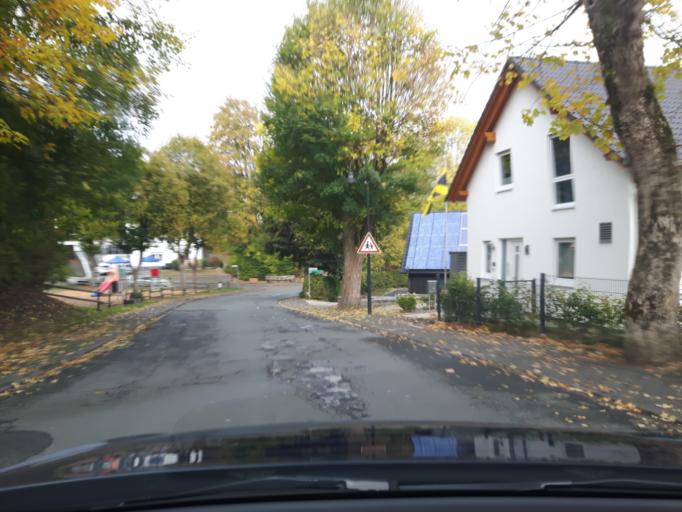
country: DE
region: North Rhine-Westphalia
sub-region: Regierungsbezirk Arnsberg
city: Bad Berleburg
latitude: 51.0557
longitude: 8.3903
